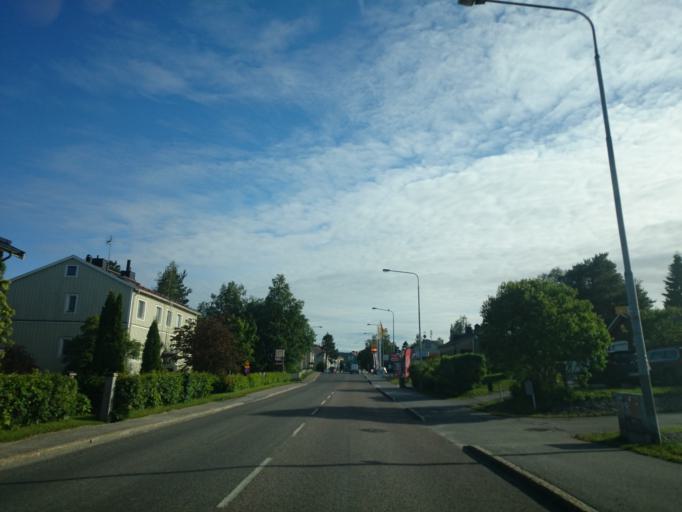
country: SE
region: Vaesternorrland
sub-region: Sundsvalls Kommun
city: Sundsvall
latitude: 62.4025
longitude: 17.3290
